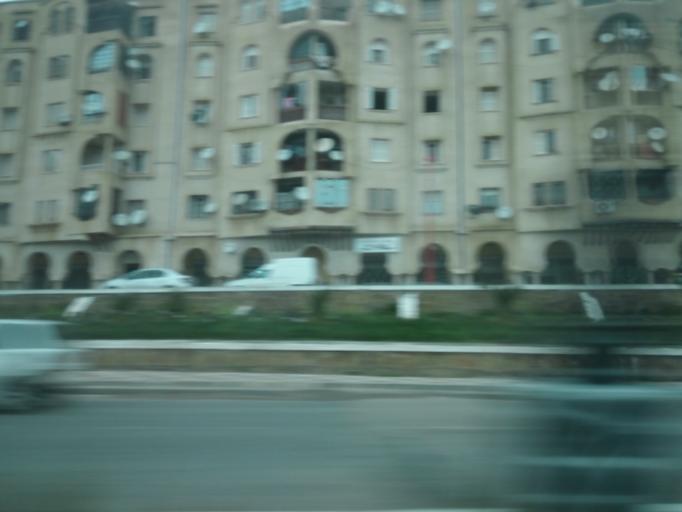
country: DZ
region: Medea
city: Medea
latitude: 36.2647
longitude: 2.7927
